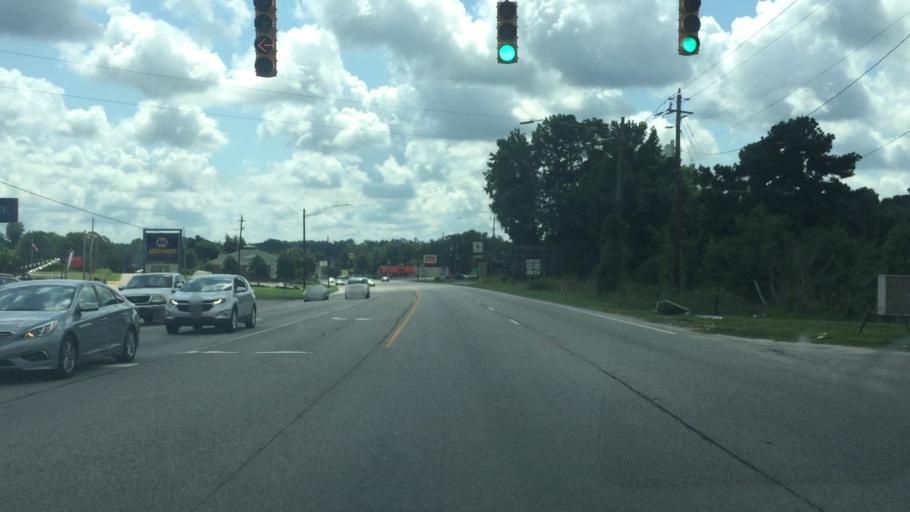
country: US
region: North Carolina
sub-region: Anson County
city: Wadesboro
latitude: 34.9650
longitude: -80.0599
